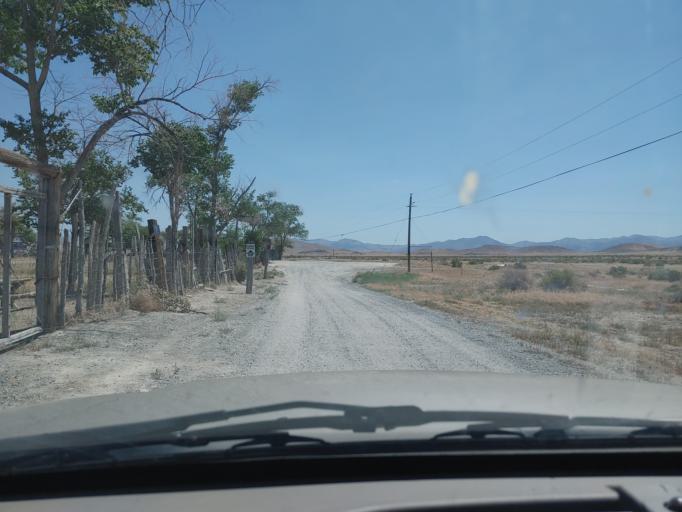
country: US
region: Nevada
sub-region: Humboldt County
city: Winnemucca
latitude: 40.6595
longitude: -118.1332
